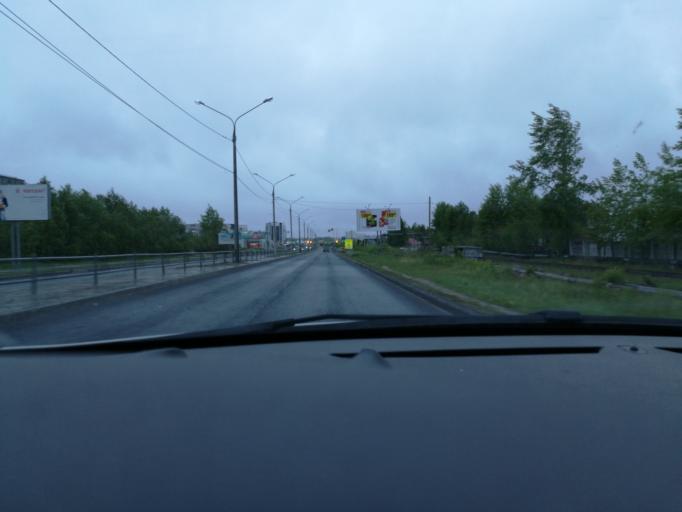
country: RU
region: Arkhangelskaya
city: Severodvinsk
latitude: 64.5647
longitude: 39.7842
